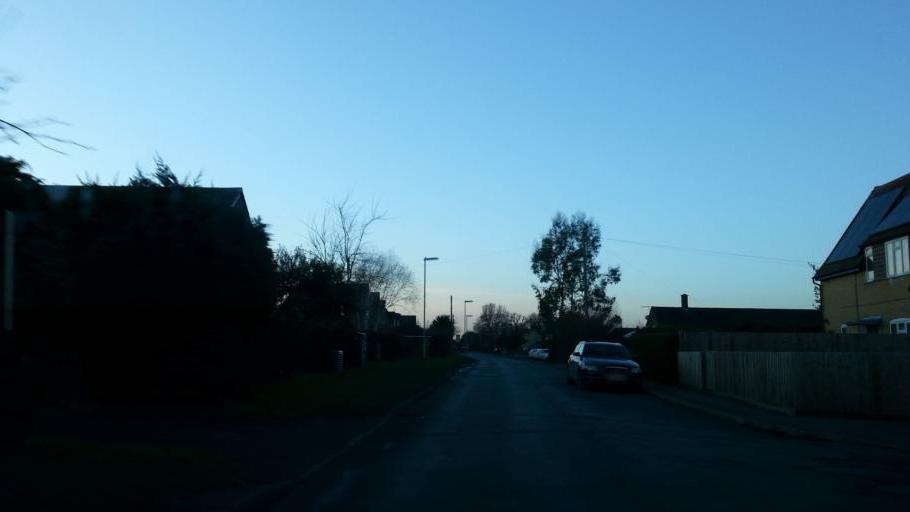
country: GB
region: England
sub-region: Cambridgeshire
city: Needingworth
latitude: 52.2972
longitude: -0.0392
